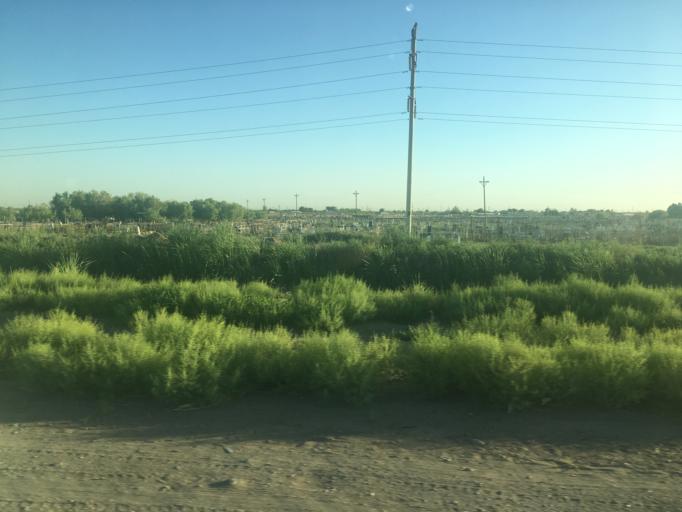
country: TM
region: Mary
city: Mary
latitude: 37.5680
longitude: 61.8093
